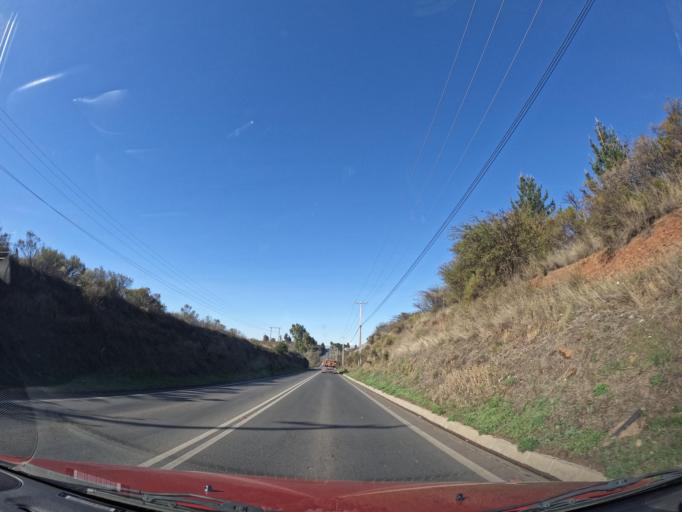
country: CL
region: Maule
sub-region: Provincia de Cauquenes
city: Cauquenes
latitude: -35.9600
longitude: -72.2610
